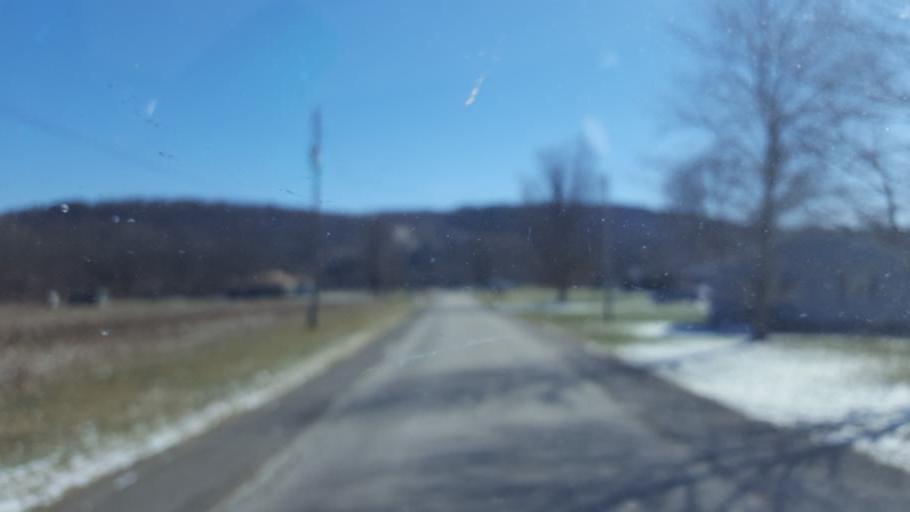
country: US
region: New York
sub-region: Allegany County
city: Wellsville
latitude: 42.0701
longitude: -77.9328
